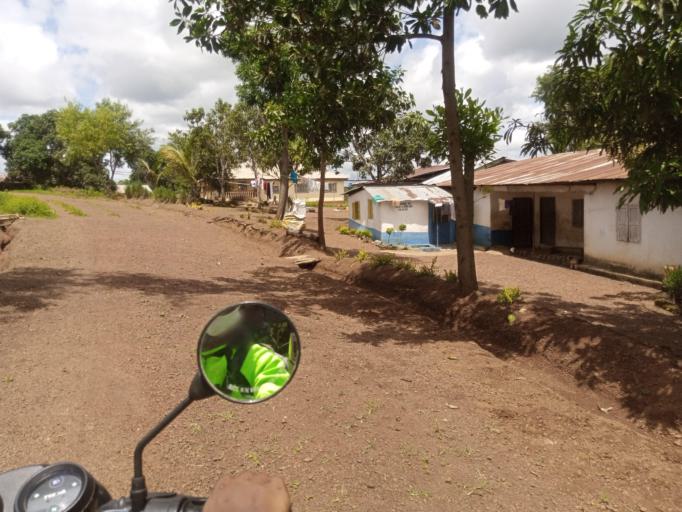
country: SL
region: Northern Province
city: Port Loko
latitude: 8.7586
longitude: -12.7799
